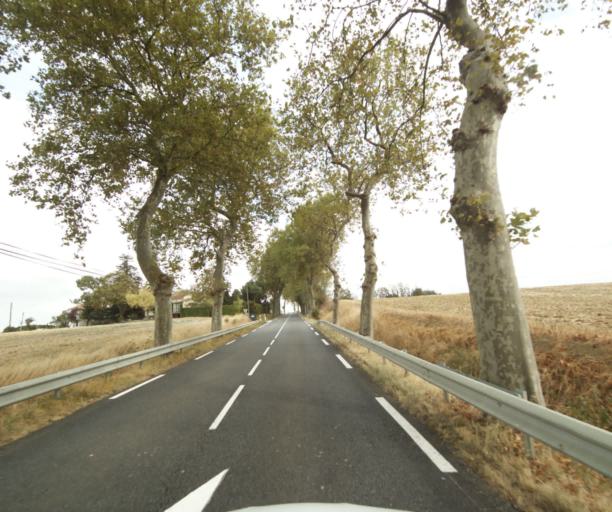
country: FR
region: Midi-Pyrenees
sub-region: Departement de la Haute-Garonne
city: Villefranche-de-Lauragais
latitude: 43.4182
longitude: 1.7181
